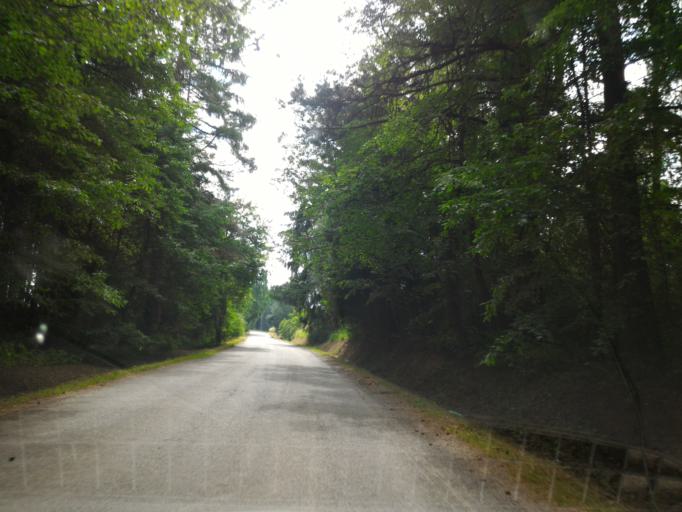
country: CZ
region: Vysocina
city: Zeletava
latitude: 49.1342
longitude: 15.5718
